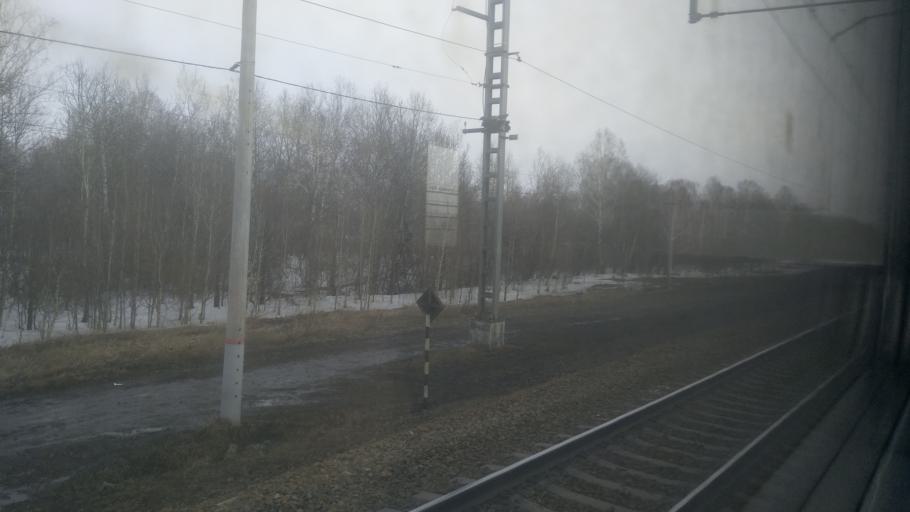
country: RU
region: Novosibirsk
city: Stantsionno-Oyashinskiy
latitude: 55.5046
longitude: 83.9193
